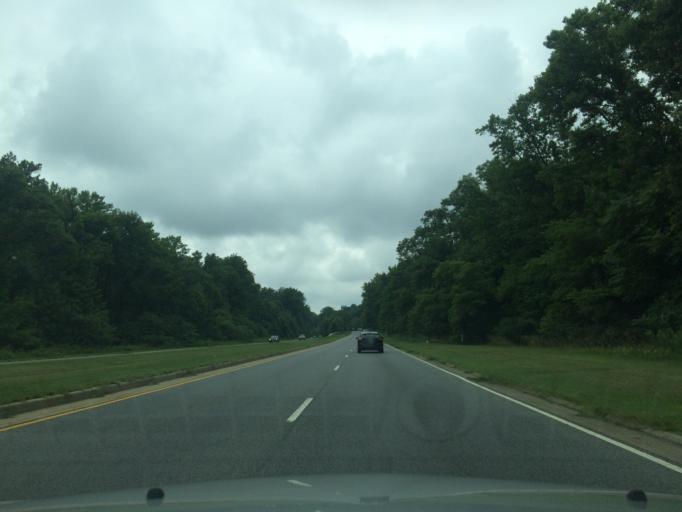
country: US
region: Maryland
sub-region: Prince George's County
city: Morningside
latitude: 38.8330
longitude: -76.8823
